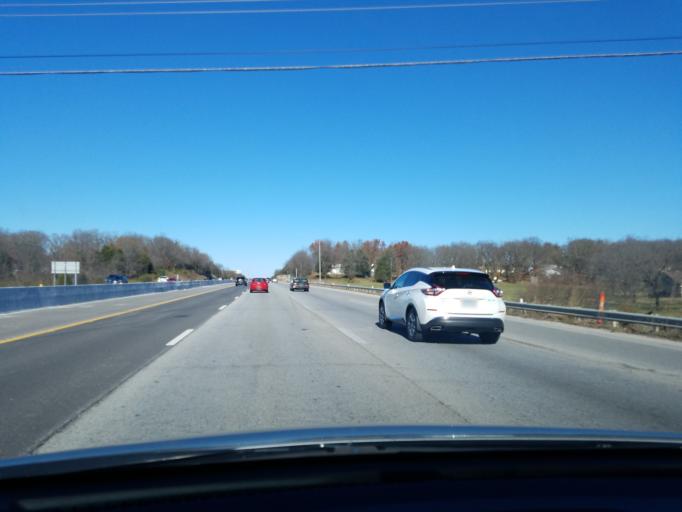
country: US
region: Missouri
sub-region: Christian County
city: Nixa
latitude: 37.1035
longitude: -93.2326
